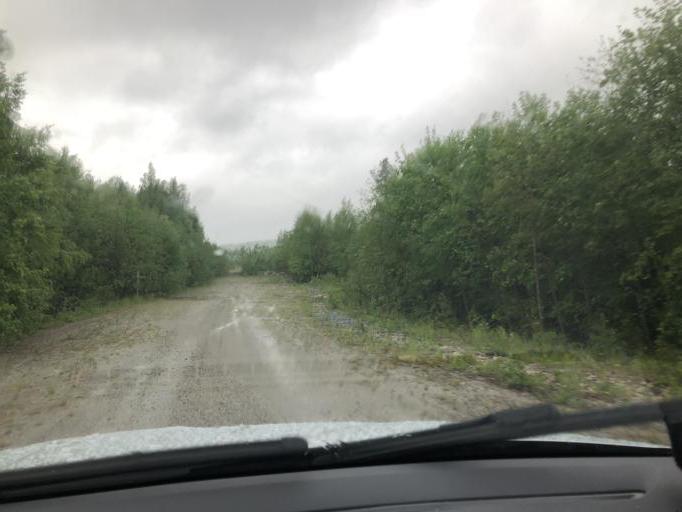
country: SE
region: Vaesternorrland
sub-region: Haernoesands Kommun
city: Haernoesand
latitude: 62.7904
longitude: 17.9270
